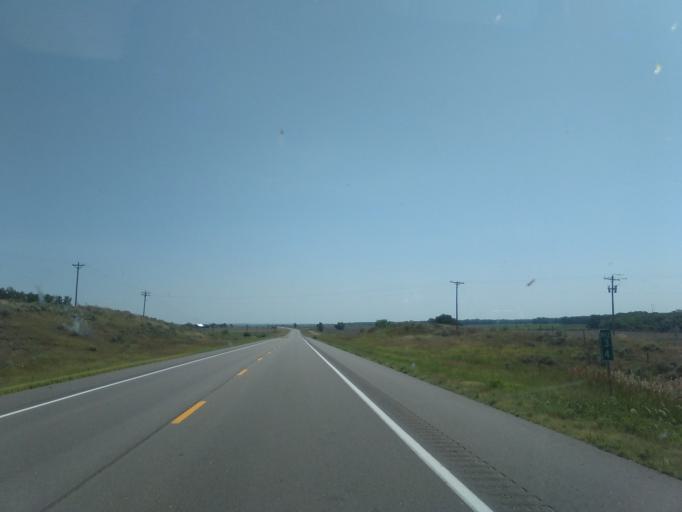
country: US
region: Nebraska
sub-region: Dundy County
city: Benkelman
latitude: 40.0803
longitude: -101.4883
